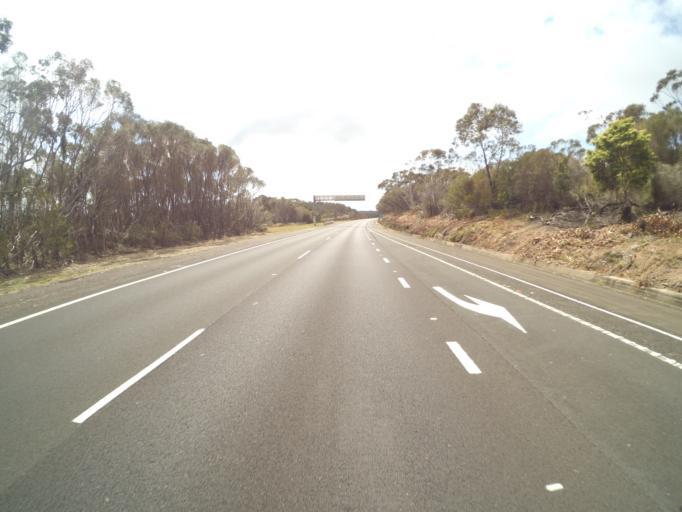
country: AU
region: New South Wales
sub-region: Wollongong
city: Bulli
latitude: -34.2949
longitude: 150.9187
